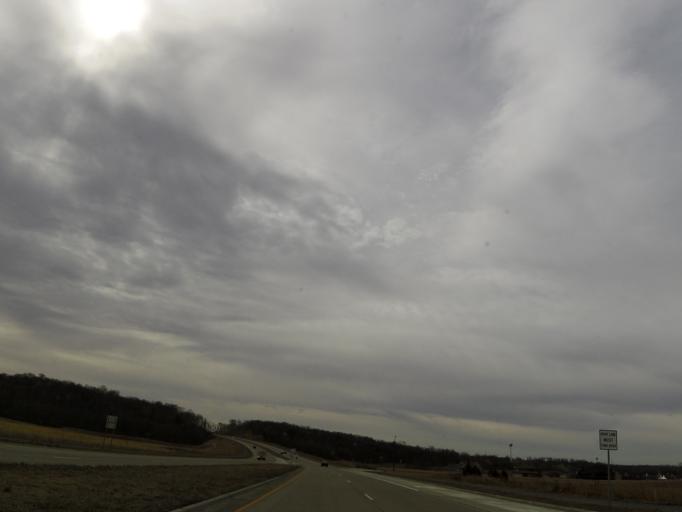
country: US
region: Minnesota
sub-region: Scott County
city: Prior Lake
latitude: 44.7633
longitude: -93.4383
